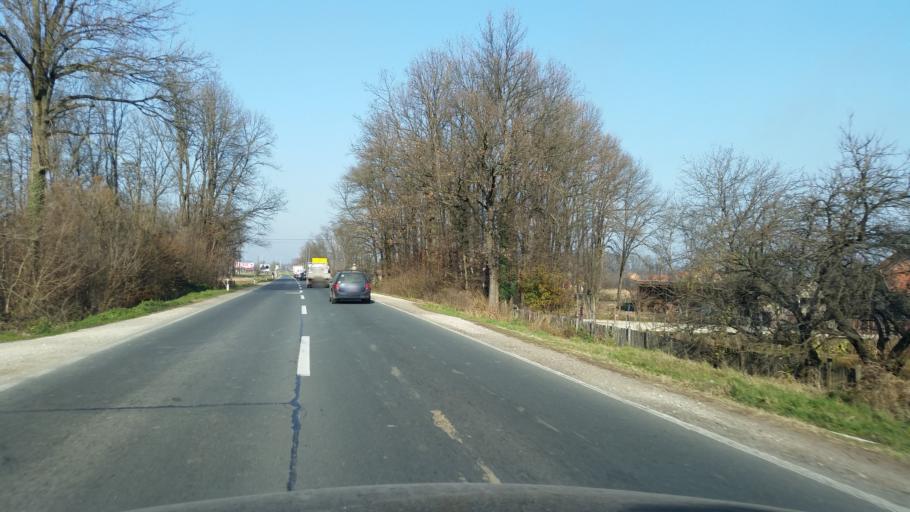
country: RS
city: Stepojevac
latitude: 44.4775
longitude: 20.2778
